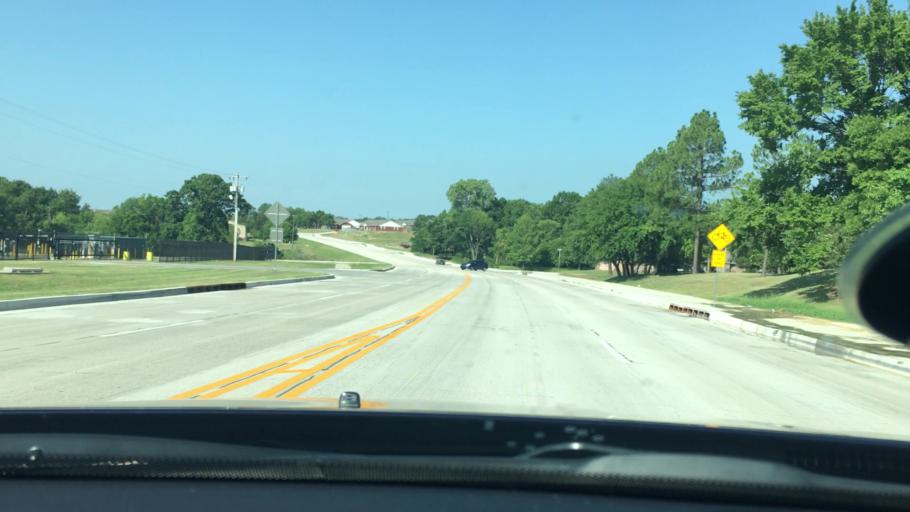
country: US
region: Oklahoma
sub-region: Pontotoc County
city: Ada
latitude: 34.7617
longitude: -96.6653
